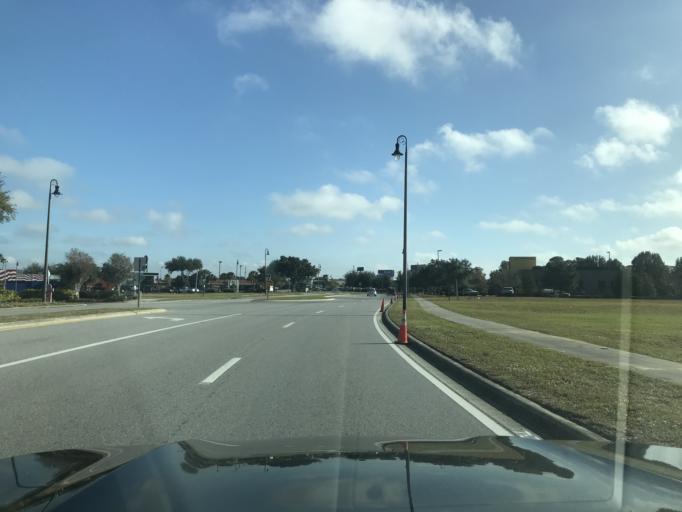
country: US
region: Florida
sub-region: Polk County
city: Citrus Ridge
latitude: 28.3391
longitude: -81.5999
